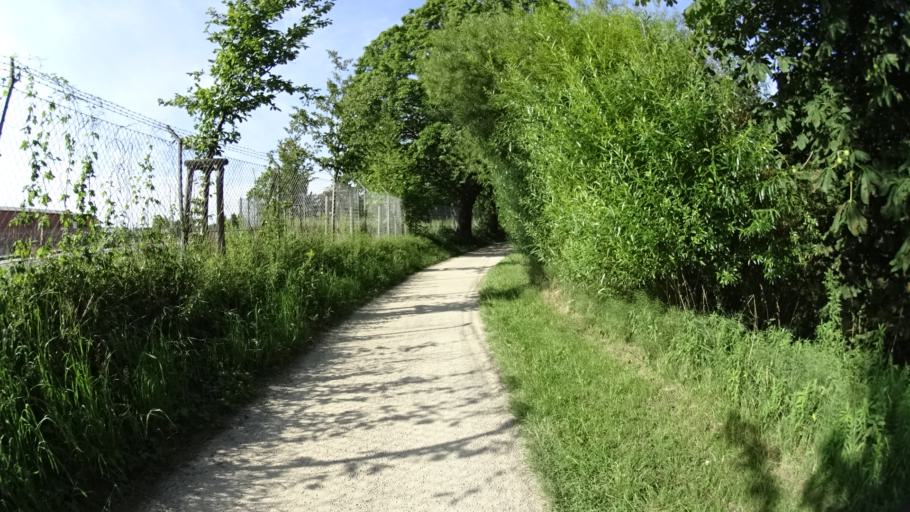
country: DE
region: Lower Saxony
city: Lueneburg
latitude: 53.2674
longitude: 10.4211
